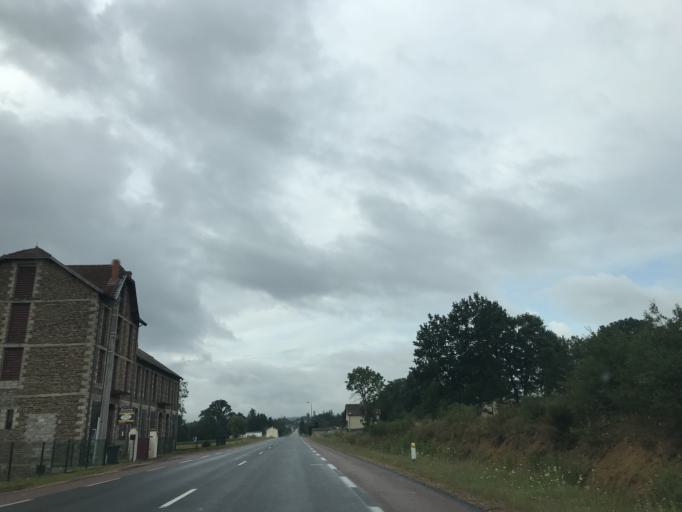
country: FR
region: Auvergne
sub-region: Departement du Puy-de-Dome
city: Arlanc
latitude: 45.4319
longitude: 3.7243
